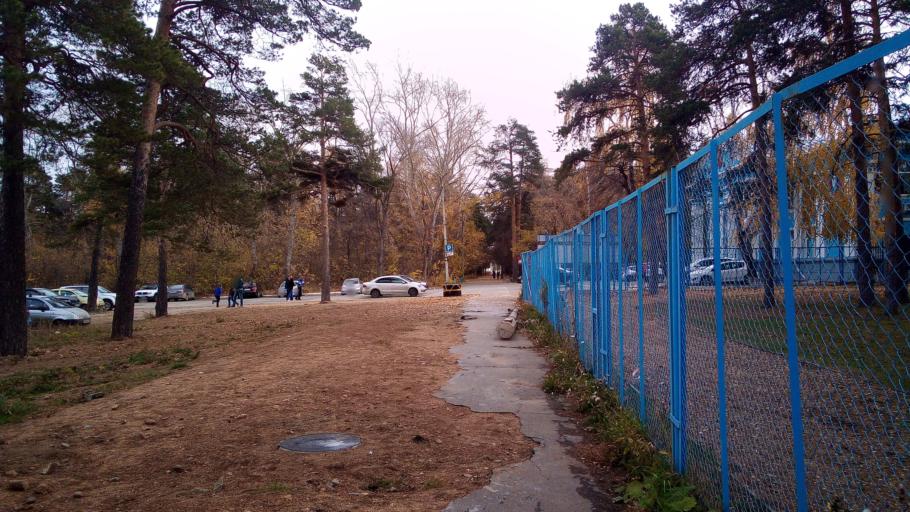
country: RU
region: Chelyabinsk
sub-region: Gorod Chelyabinsk
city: Chelyabinsk
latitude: 55.1650
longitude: 61.3755
